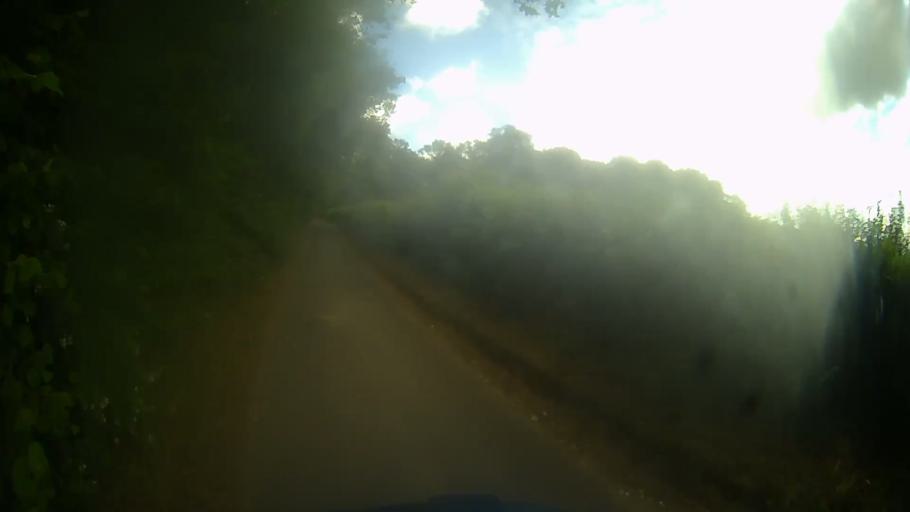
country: GB
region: England
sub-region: Hampshire
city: Andover
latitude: 51.2442
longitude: -1.4449
